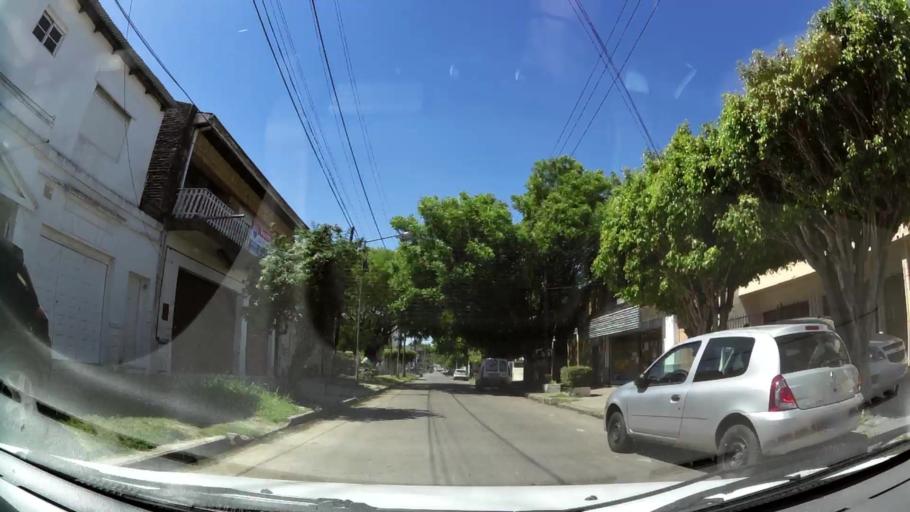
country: AR
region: Buenos Aires
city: Caseros
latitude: -34.5691
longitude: -58.5702
